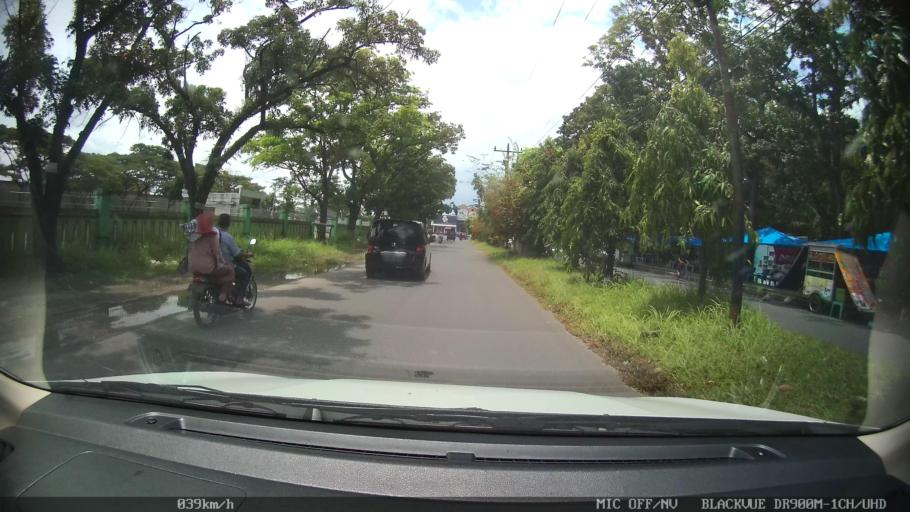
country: ID
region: North Sumatra
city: Medan
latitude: 3.6144
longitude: 98.7084
